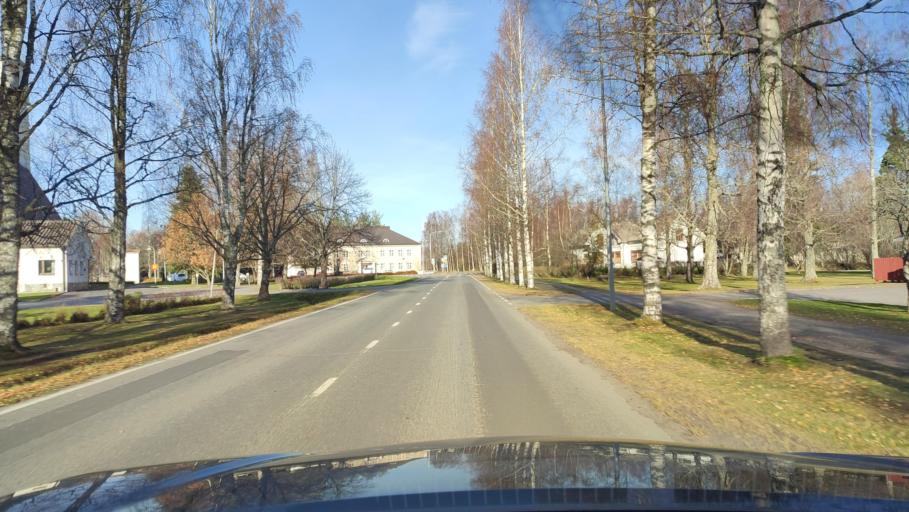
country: FI
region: Southern Ostrobothnia
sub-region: Suupohja
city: Teuva
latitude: 62.4783
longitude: 21.7400
